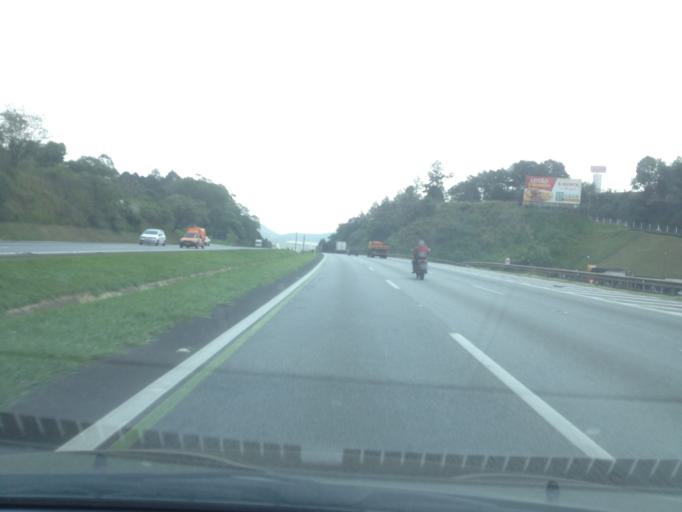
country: BR
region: Sao Paulo
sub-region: Pirapora Do Bom Jesus
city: Pirapora do Bom Jesus
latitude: -23.4363
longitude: -47.0765
